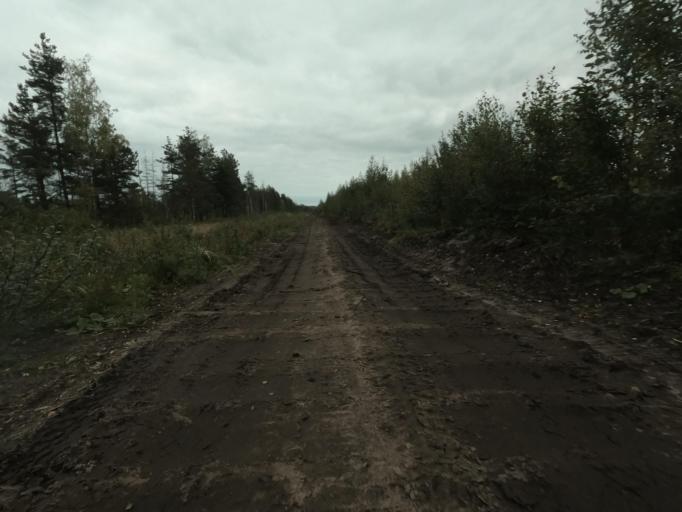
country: RU
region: St.-Petersburg
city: Sapernyy
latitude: 59.7613
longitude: 30.7186
